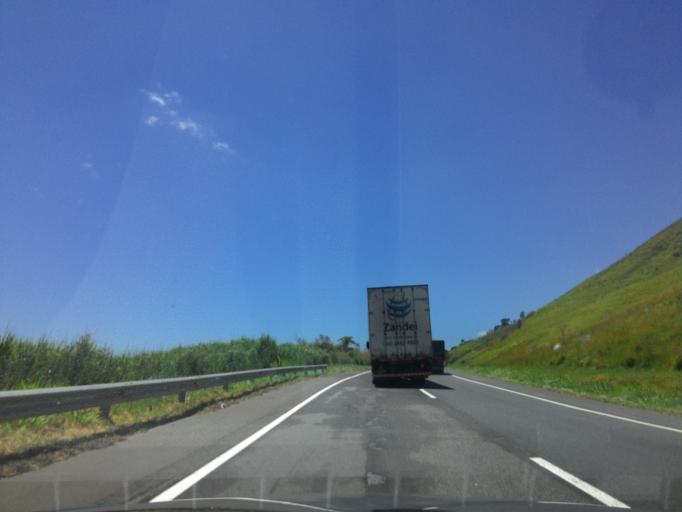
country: BR
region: Sao Paulo
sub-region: Cajati
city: Cajati
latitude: -24.9698
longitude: -48.4878
